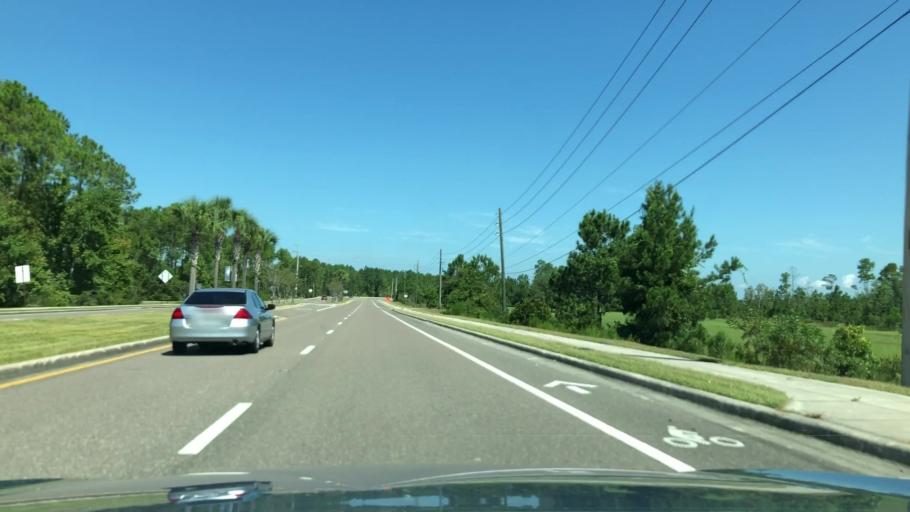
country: US
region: Florida
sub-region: Saint Johns County
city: Fruit Cove
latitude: 30.0878
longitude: -81.5330
